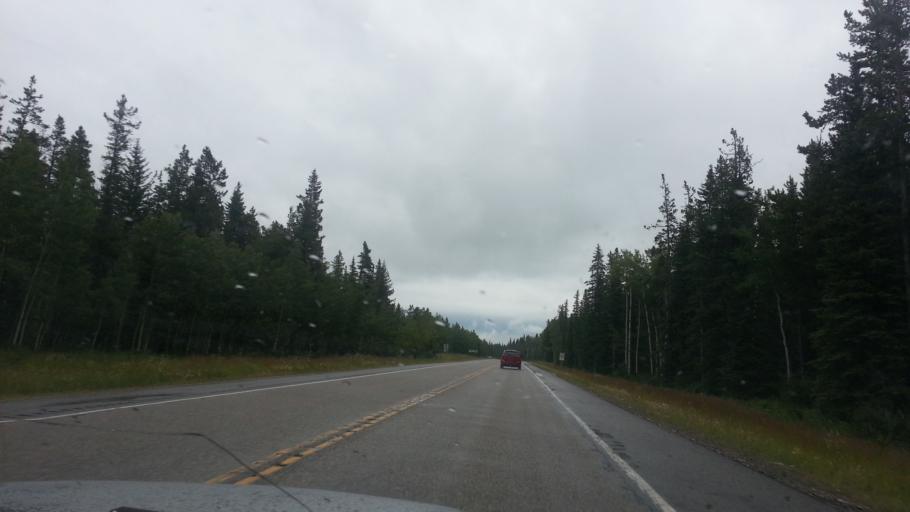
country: CA
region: Alberta
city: Cochrane
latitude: 50.9096
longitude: -114.6547
